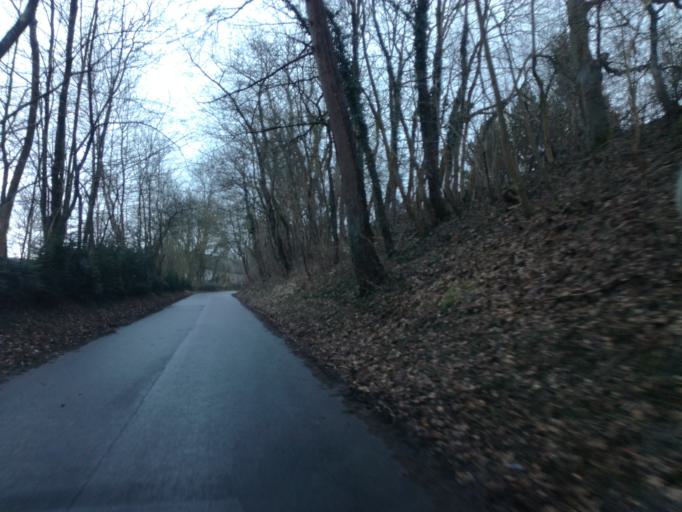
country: DK
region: South Denmark
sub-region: Vejle Kommune
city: Borkop
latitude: 55.6187
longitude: 9.6680
